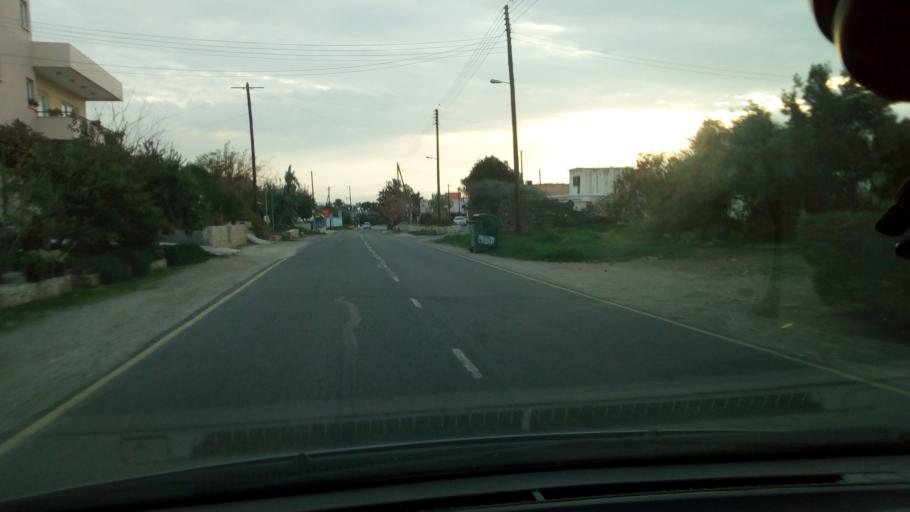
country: CY
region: Pafos
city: Polis
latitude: 35.1209
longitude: 32.5139
